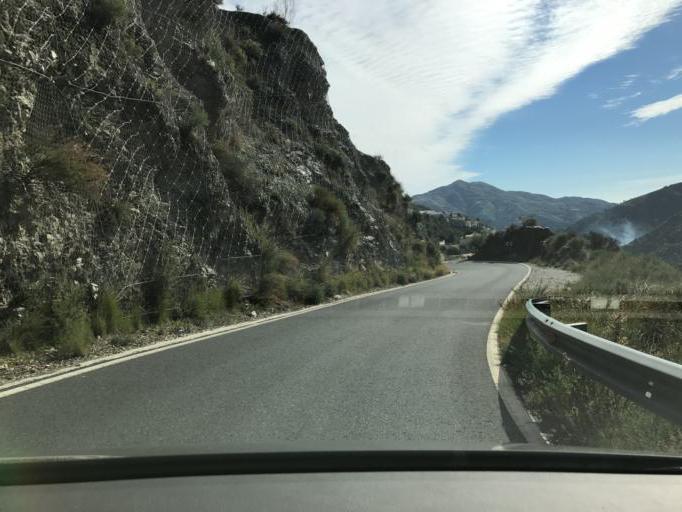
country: ES
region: Andalusia
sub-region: Provincia de Granada
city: Otivar
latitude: 36.8271
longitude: -3.6879
